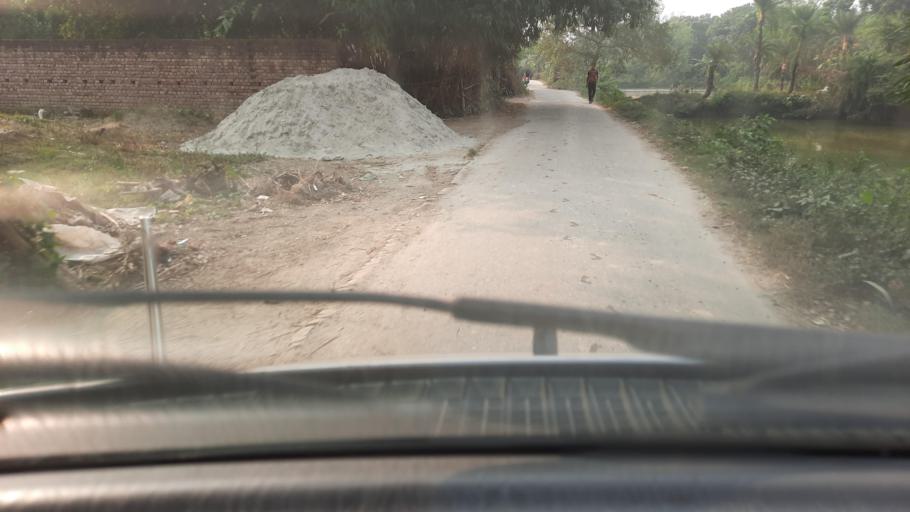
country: BD
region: Khulna
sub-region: Chuadanga
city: Nowlamary
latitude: 23.5996
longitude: 88.8434
